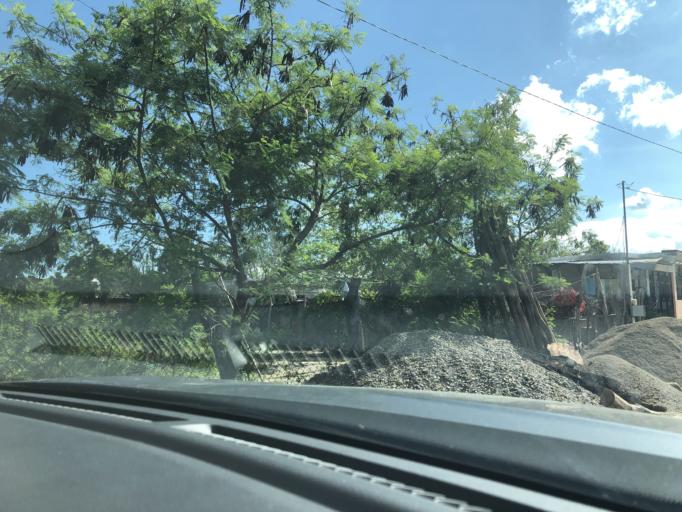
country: MX
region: Oaxaca
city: San Jeronimo Ixtepec
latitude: 16.5589
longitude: -95.1054
